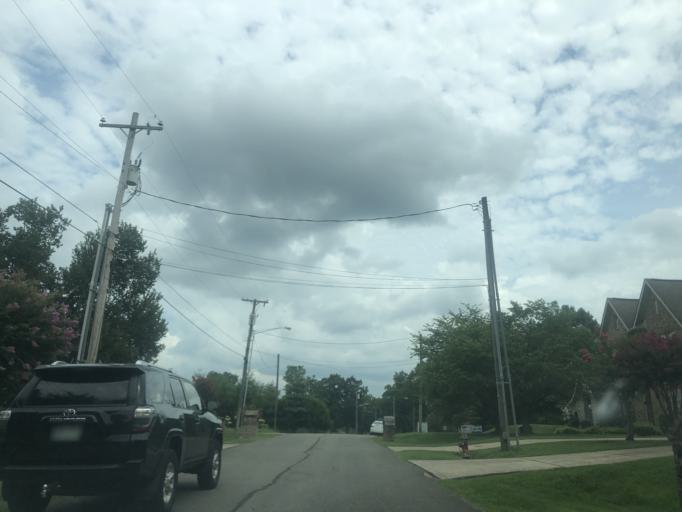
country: US
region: Tennessee
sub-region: Davidson County
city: Oak Hill
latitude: 36.0968
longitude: -86.7985
